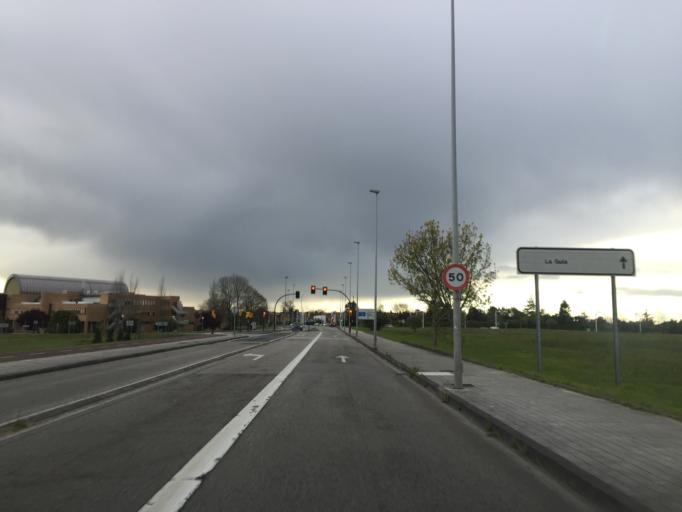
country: ES
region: Asturias
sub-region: Province of Asturias
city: Gijon
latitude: 43.5257
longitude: -5.6257
